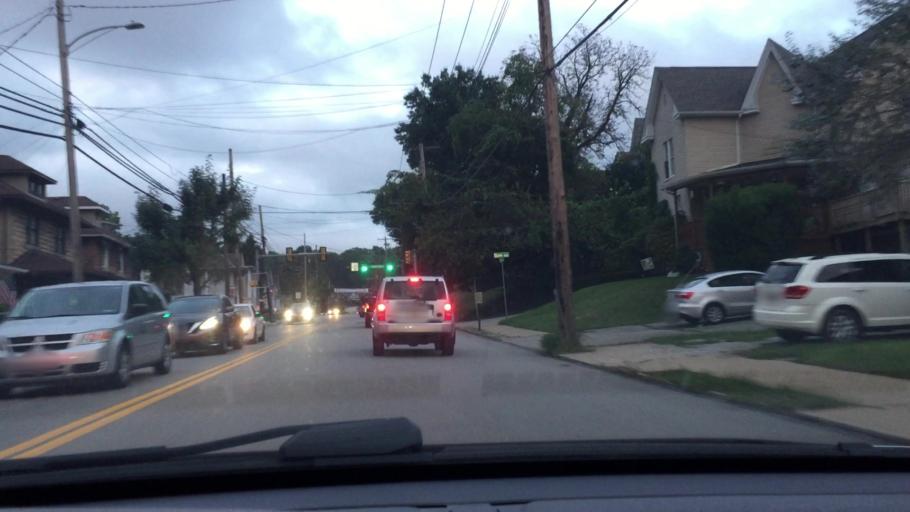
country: US
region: Pennsylvania
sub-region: Washington County
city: East Washington
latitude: 40.1627
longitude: -80.2257
